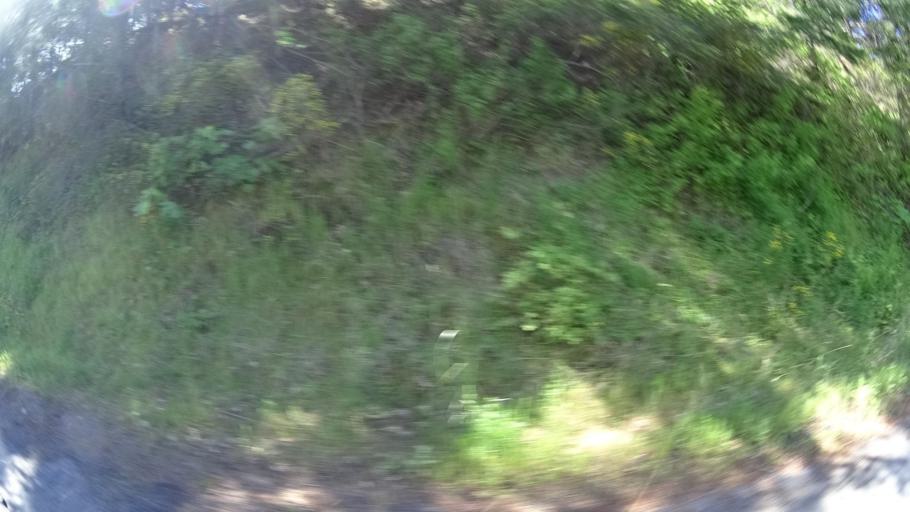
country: US
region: California
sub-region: Humboldt County
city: Rio Dell
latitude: 40.2757
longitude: -124.2411
